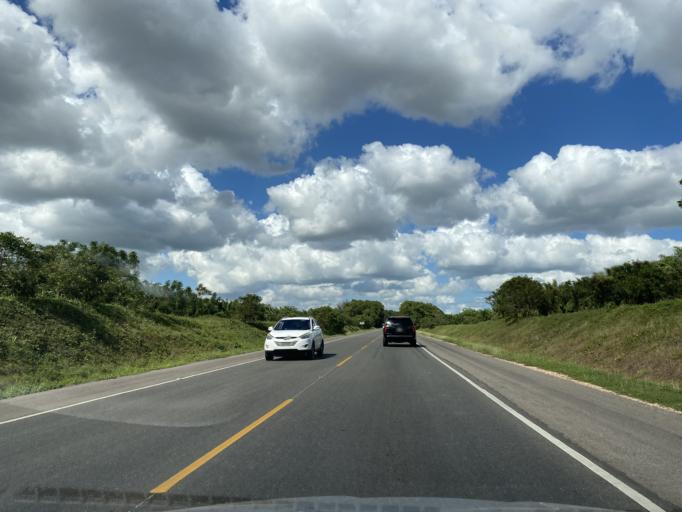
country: DO
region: Monte Plata
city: Monte Plata
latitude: 18.7447
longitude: -69.7649
